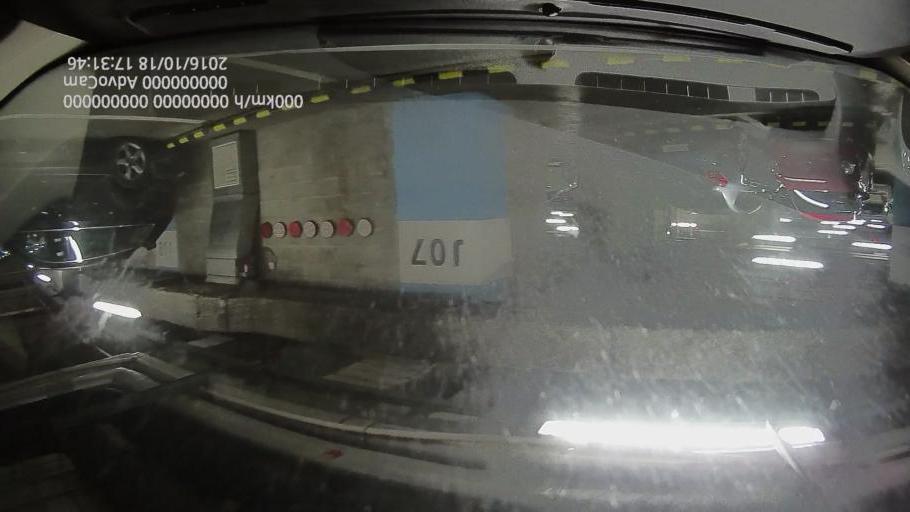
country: RO
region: Ilfov
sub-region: Comuna Otopeni
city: Otopeni
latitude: 44.5044
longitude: 26.0894
